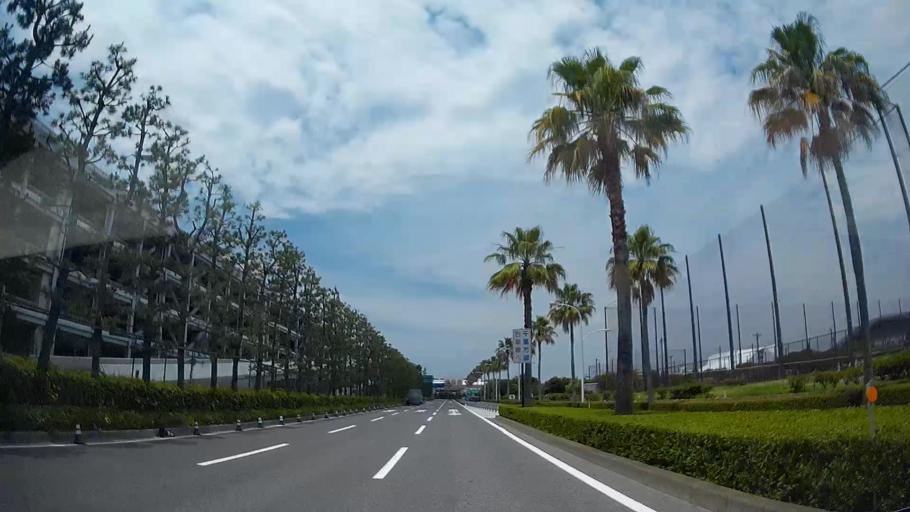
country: JP
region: Tokyo
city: Urayasu
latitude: 35.6279
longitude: 139.8907
